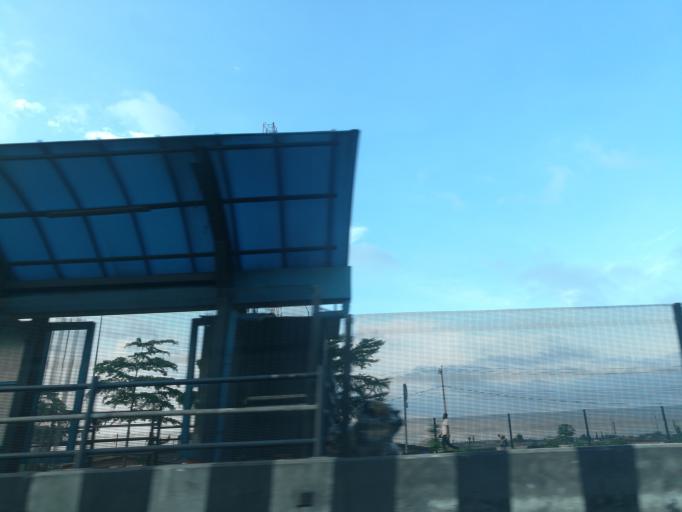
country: NG
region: Lagos
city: Ebute Ikorodu
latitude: 6.6195
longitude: 3.4733
